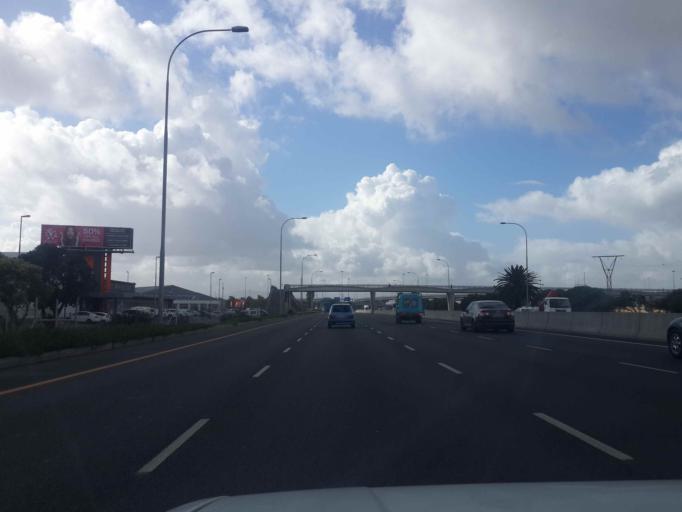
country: ZA
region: Western Cape
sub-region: City of Cape Town
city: Rosebank
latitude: -33.9187
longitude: 18.4744
